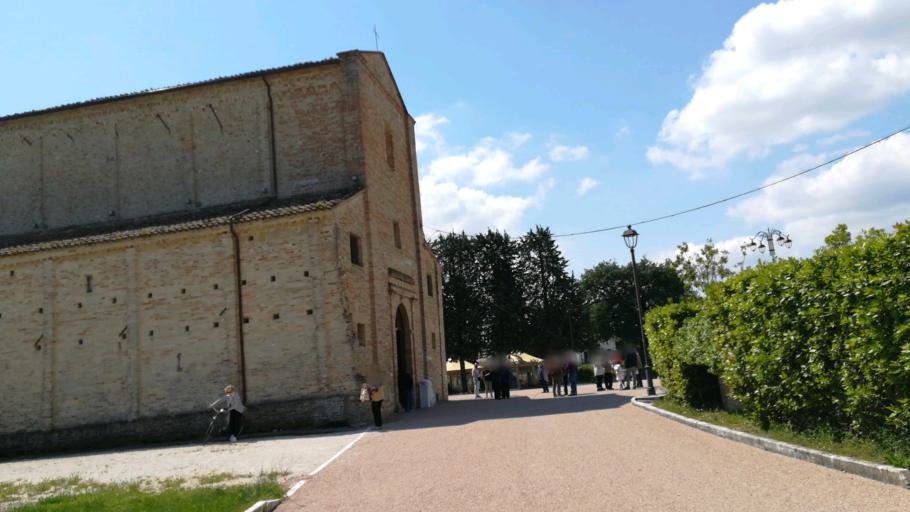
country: IT
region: The Marches
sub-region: Provincia di Macerata
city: Borgo Stazione
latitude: 43.2807
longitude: 13.6395
